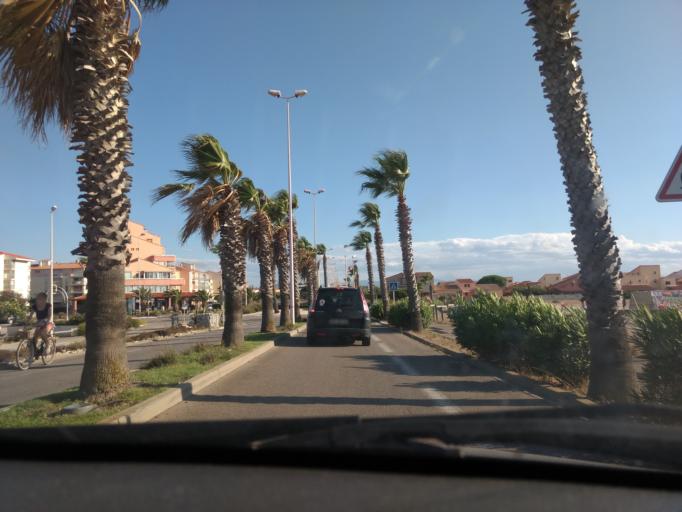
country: FR
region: Languedoc-Roussillon
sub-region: Departement des Pyrenees-Orientales
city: Le Barcares
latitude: 42.7970
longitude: 3.0366
